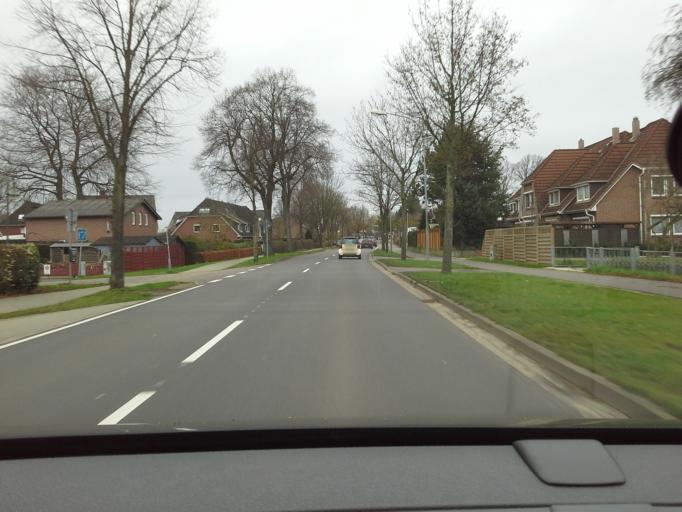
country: DE
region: Schleswig-Holstein
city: Kummerfeld
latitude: 53.6893
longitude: 9.7912
